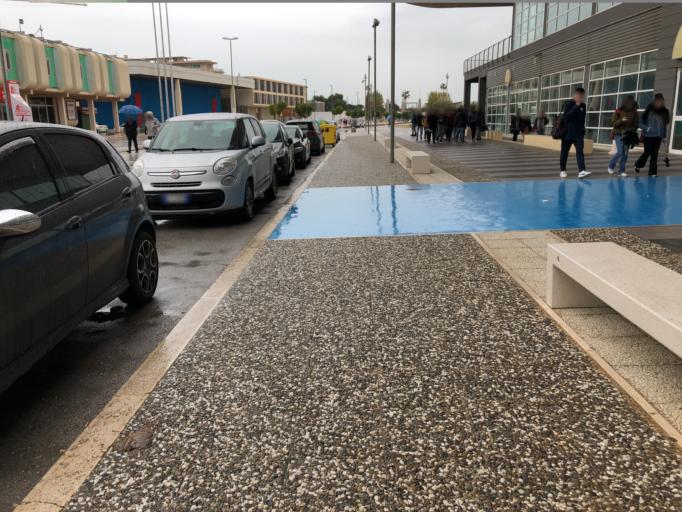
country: IT
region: Apulia
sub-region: Provincia di Bari
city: Bari
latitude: 41.1354
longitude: 16.8403
